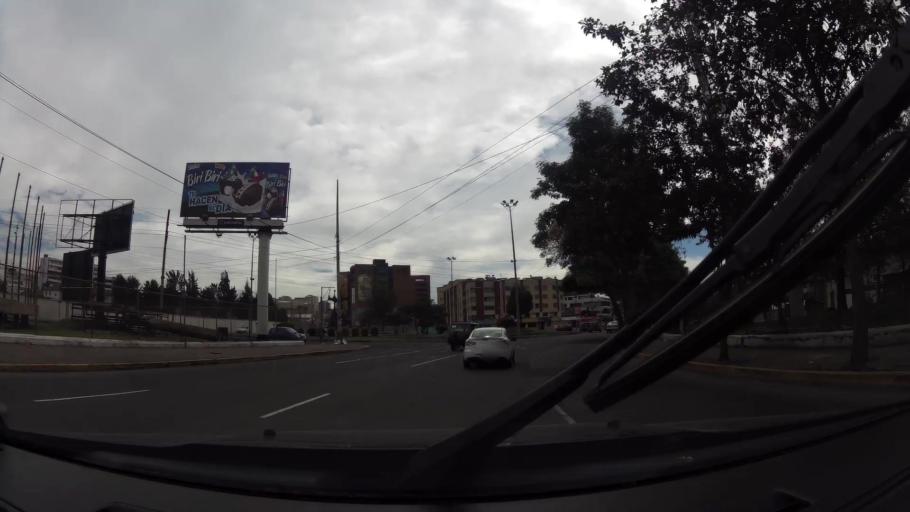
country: EC
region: Pichincha
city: Quito
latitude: -0.2133
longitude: -78.4891
